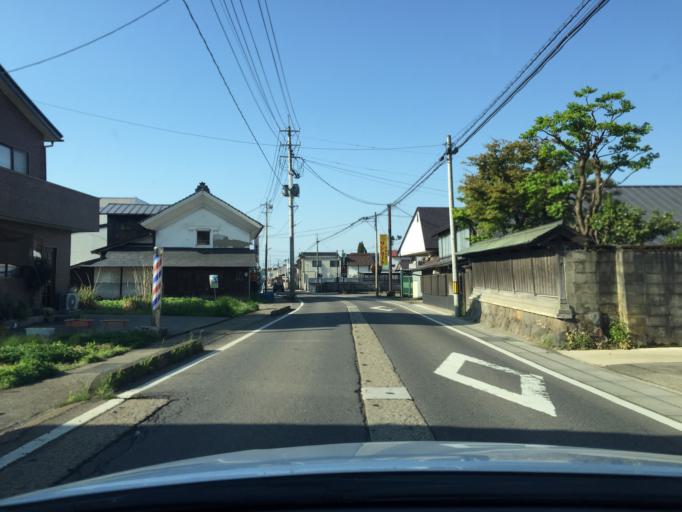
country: JP
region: Fukushima
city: Kitakata
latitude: 37.6752
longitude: 139.8717
